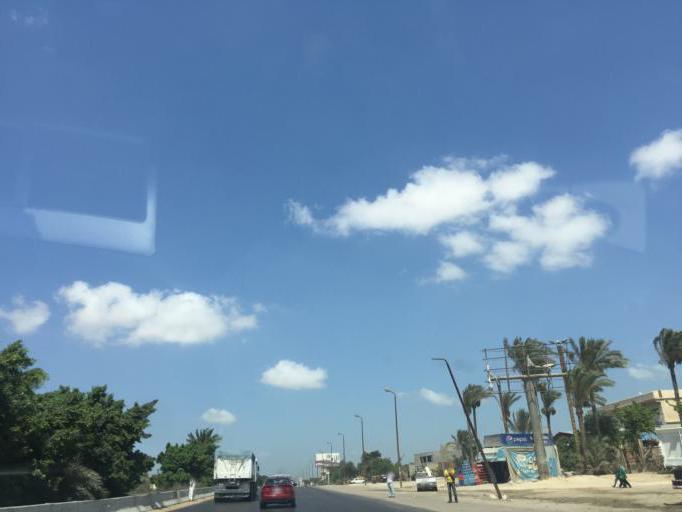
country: EG
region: Alexandria
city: Alexandria
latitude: 31.0481
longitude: 29.7896
